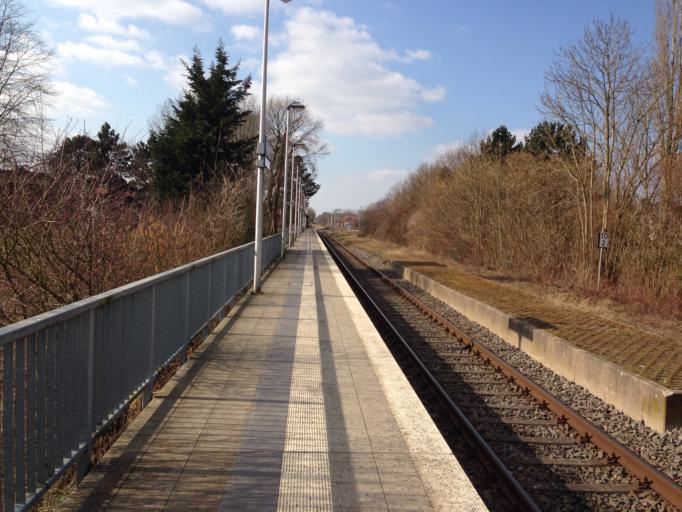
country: DE
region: North Rhine-Westphalia
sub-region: Regierungsbezirk Munster
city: Greven
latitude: 52.0214
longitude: 7.5642
